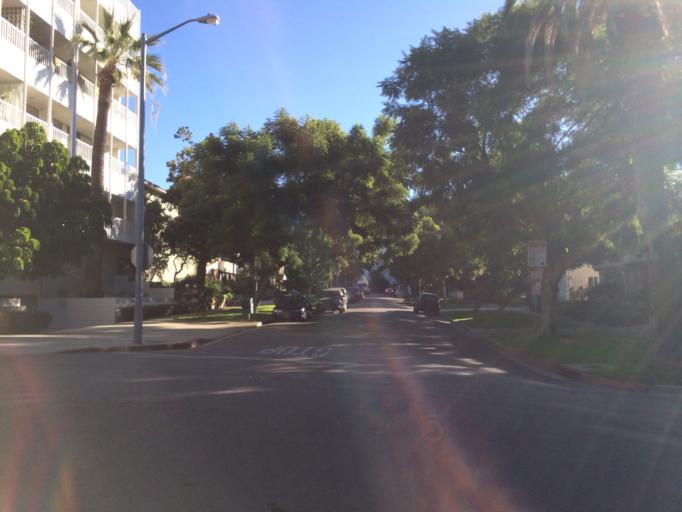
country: US
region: California
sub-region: Los Angeles County
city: West Hollywood
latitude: 34.0954
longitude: -118.3704
